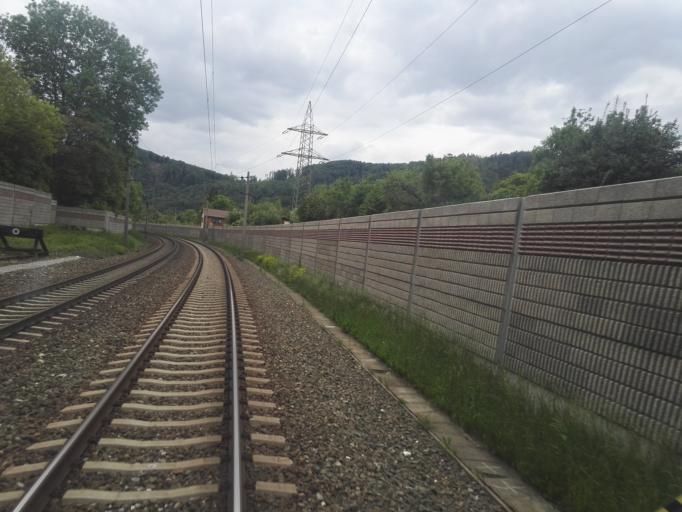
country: AT
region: Styria
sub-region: Graz Stadt
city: Goesting
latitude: 47.1040
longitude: 15.3968
